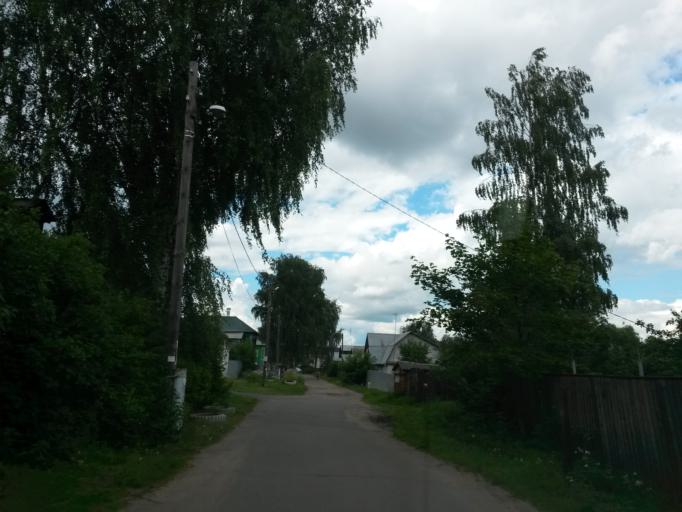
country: RU
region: Jaroslavl
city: Yaroslavl
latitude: 57.6049
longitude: 39.8910
